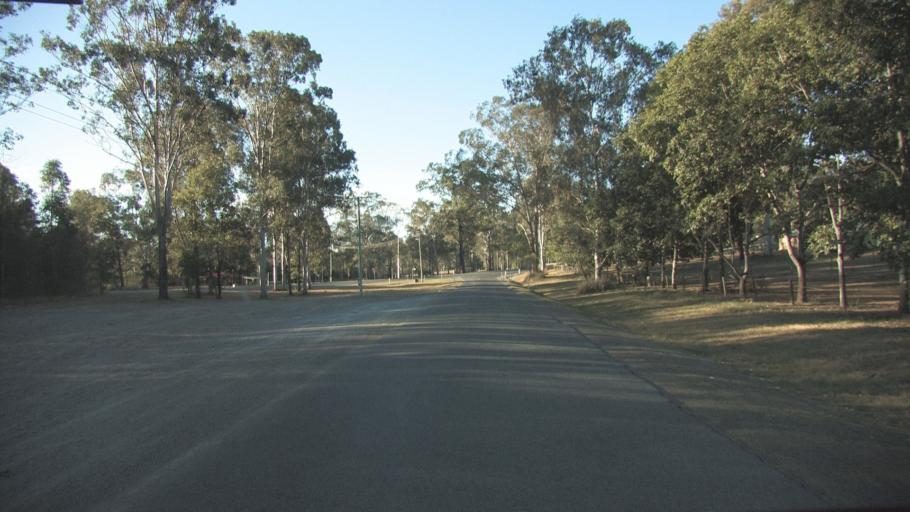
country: AU
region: Queensland
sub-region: Logan
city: Cedar Vale
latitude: -27.8617
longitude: 152.9781
